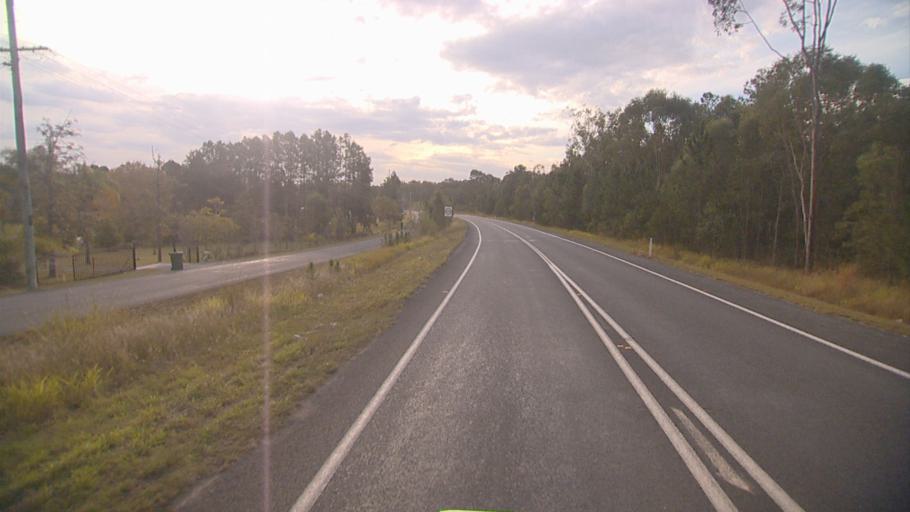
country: AU
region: Queensland
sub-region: Logan
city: Cedar Vale
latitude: -27.8440
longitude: 153.1186
